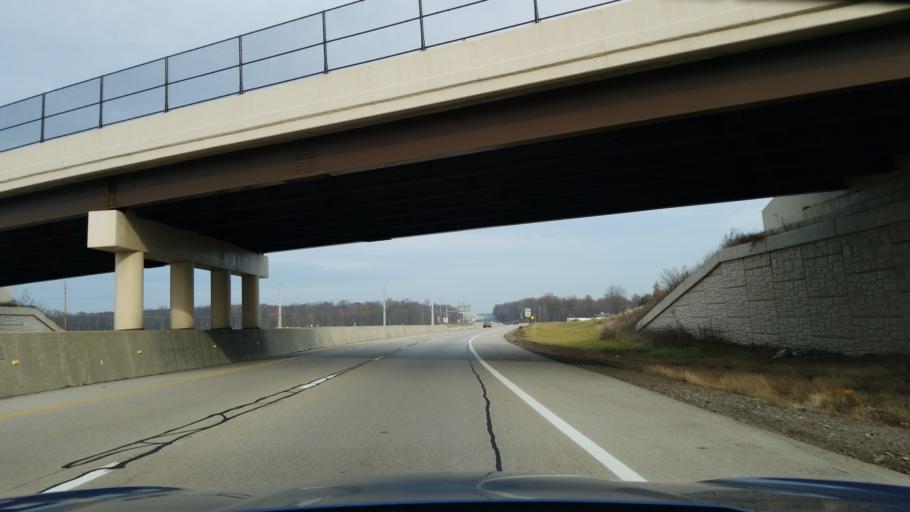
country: US
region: Ohio
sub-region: Summit County
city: Boston Heights
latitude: 41.2624
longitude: -81.5024
